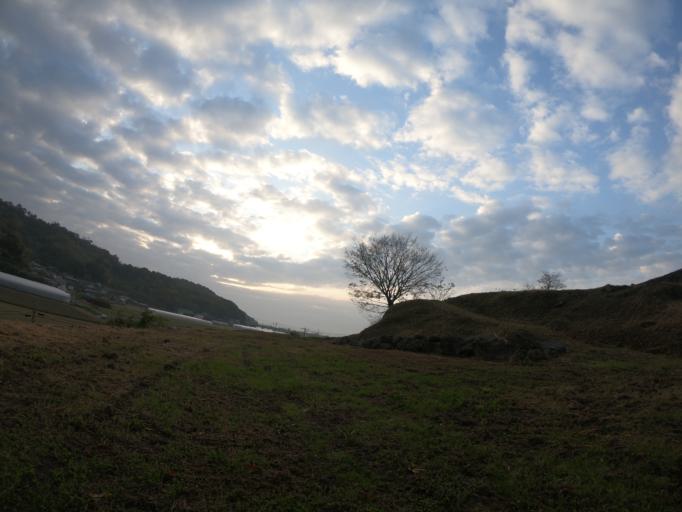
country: JP
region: Nagasaki
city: Shimabara
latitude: 32.6594
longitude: 130.2554
